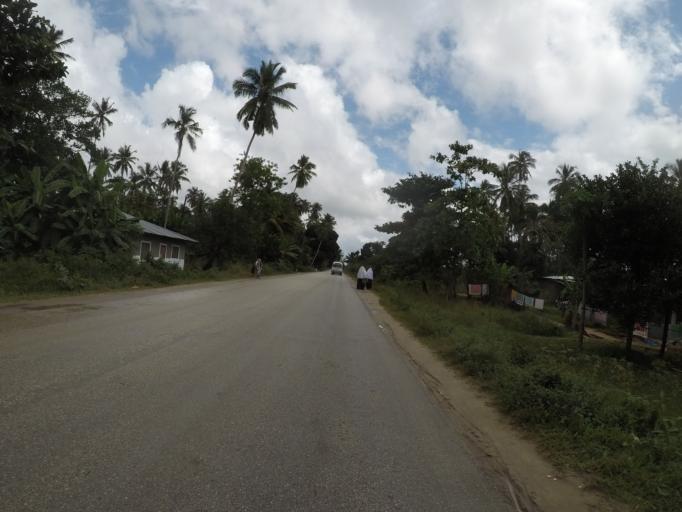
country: TZ
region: Zanzibar North
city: Gamba
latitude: -5.9652
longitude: 39.2527
